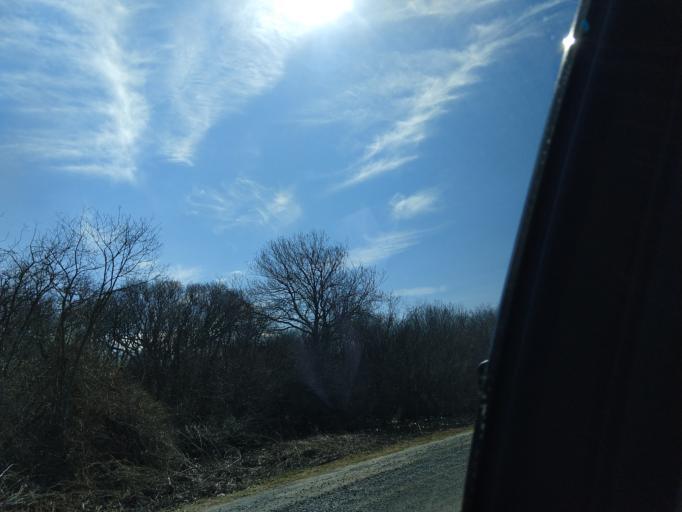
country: US
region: Massachusetts
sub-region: Essex County
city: Ipswich
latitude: 42.7152
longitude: -70.7789
